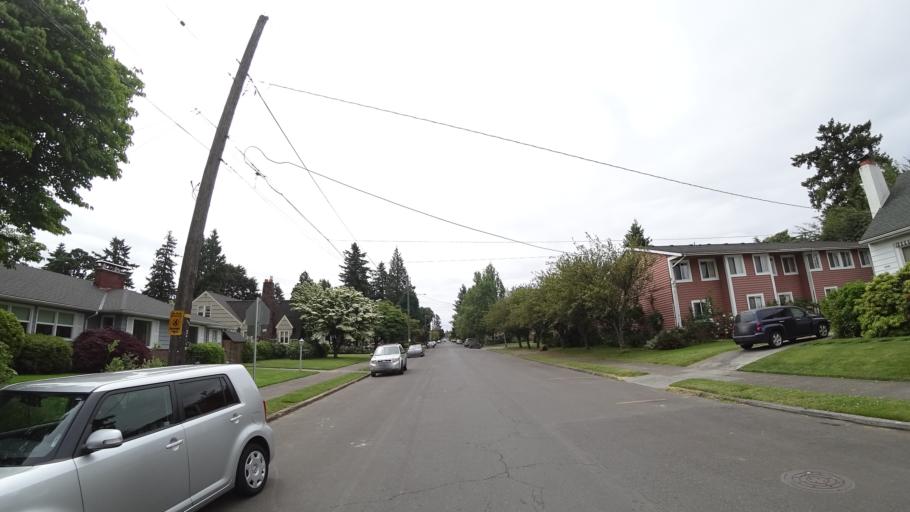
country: US
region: Oregon
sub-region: Multnomah County
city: Portland
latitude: 45.5697
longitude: -122.6350
